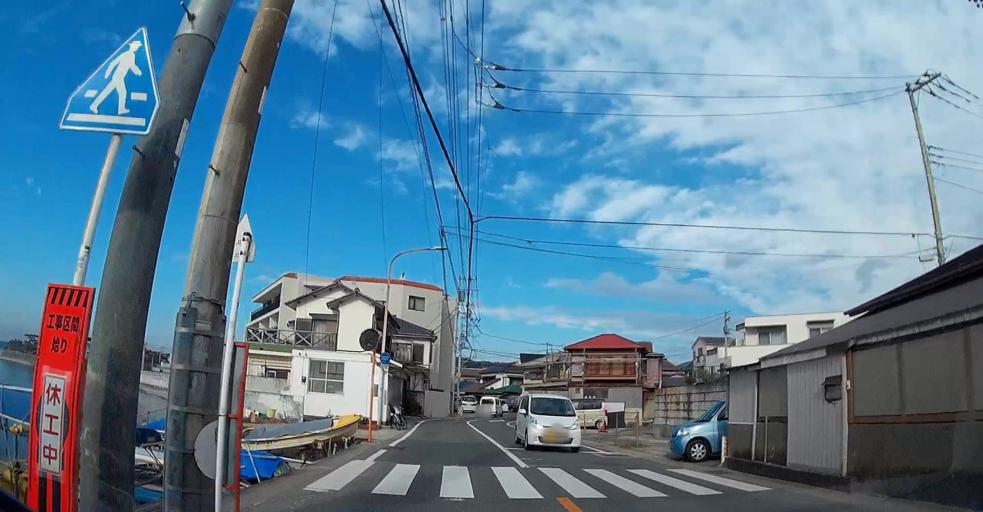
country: JP
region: Kanagawa
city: Hayama
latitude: 35.2702
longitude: 139.5711
